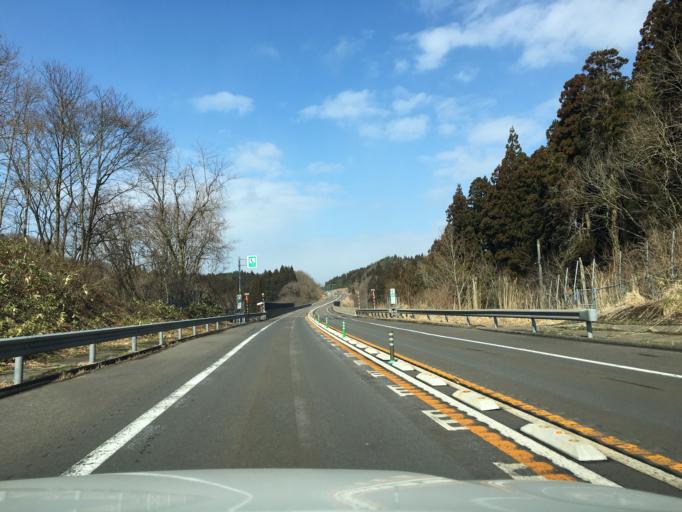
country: JP
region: Akita
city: Akita
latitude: 39.7438
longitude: 140.1612
